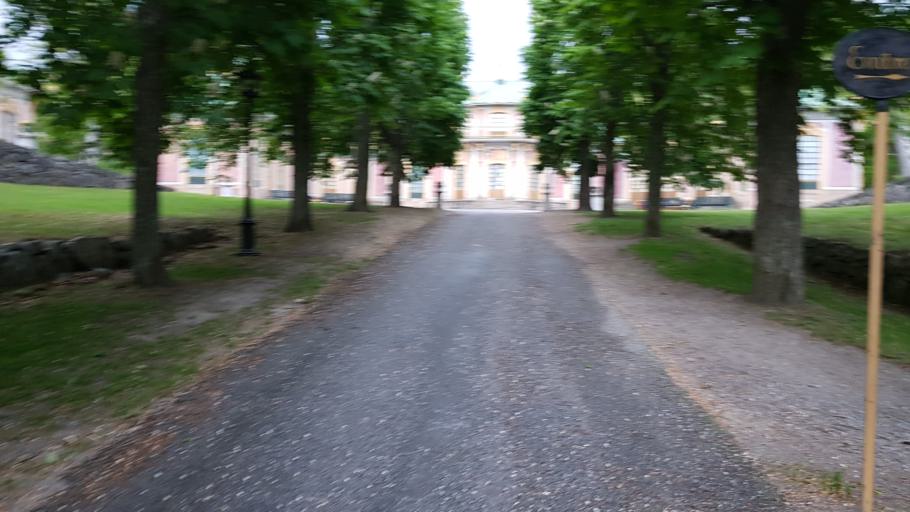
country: SE
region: Stockholm
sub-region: Stockholms Kommun
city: Bromma
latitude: 59.3176
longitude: 17.8780
